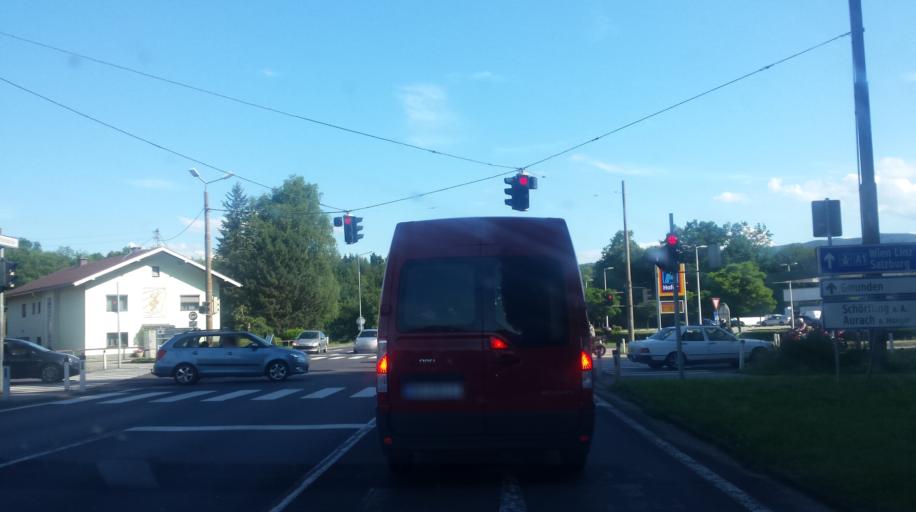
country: AT
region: Upper Austria
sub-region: Politischer Bezirk Vocklabruck
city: Attnang-Puchheim
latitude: 47.9830
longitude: 13.6987
